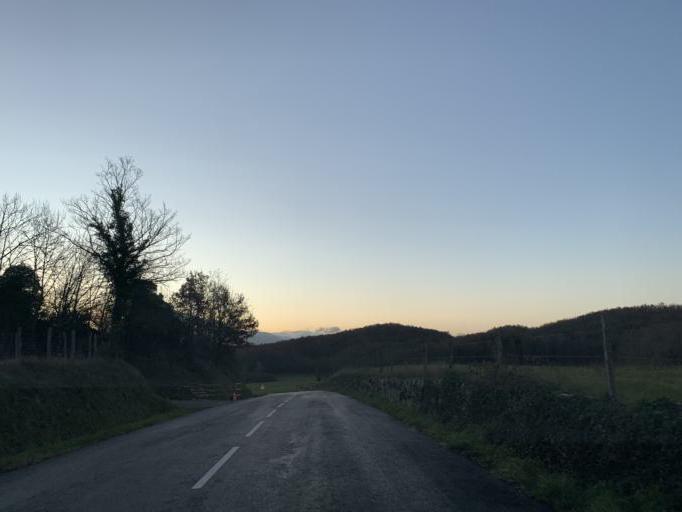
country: FR
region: Rhone-Alpes
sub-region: Departement de l'Ain
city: Belley
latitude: 45.7903
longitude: 5.6446
